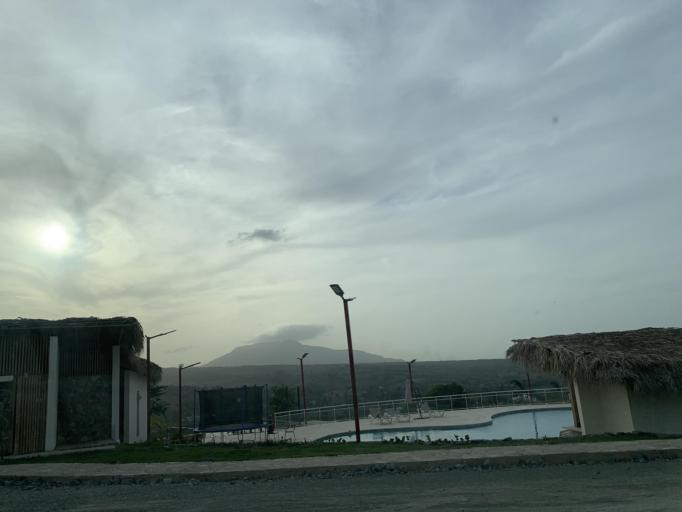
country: DO
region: Santiago
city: Pedro Garcia
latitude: 19.7008
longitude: -70.6140
